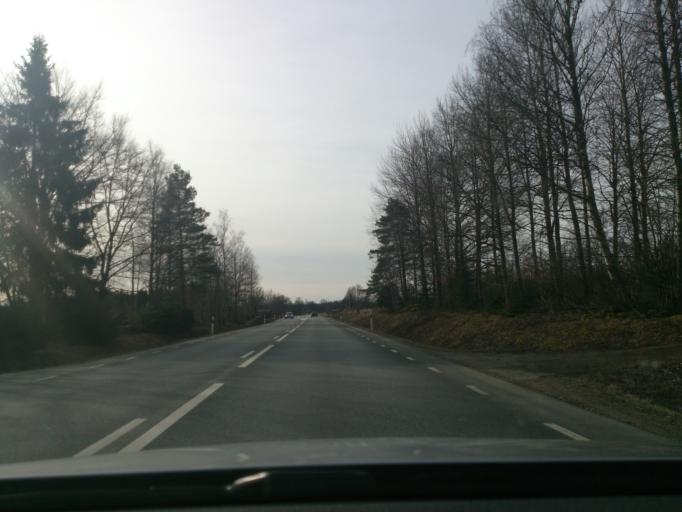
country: SE
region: Kronoberg
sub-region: Alvesta Kommun
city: Moheda
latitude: 56.9670
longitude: 14.5712
